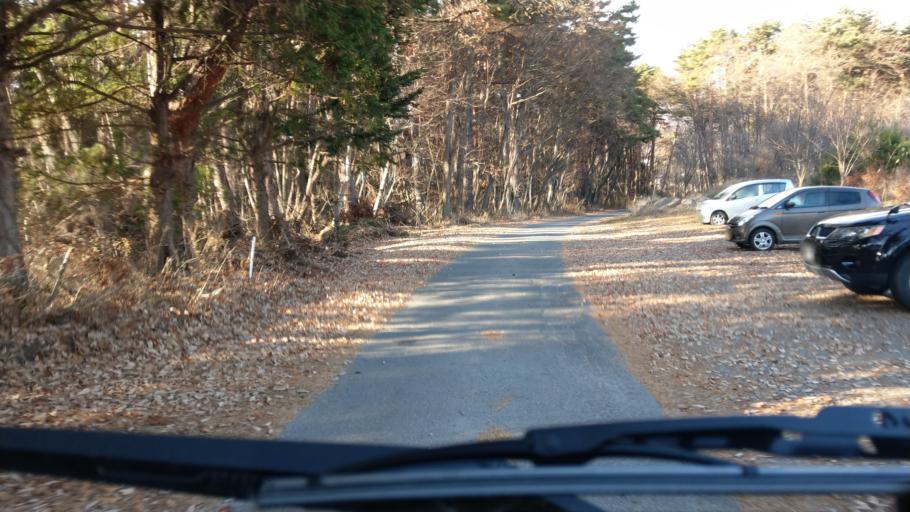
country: JP
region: Nagano
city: Komoro
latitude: 36.3478
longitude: 138.4497
